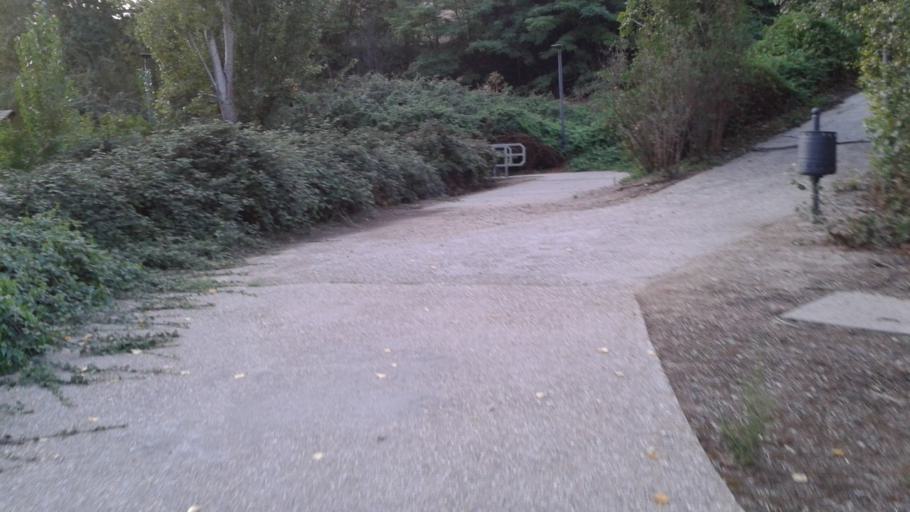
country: ES
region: Castille and Leon
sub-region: Provincia de Valladolid
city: Arroyo
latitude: 41.6088
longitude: -4.8017
